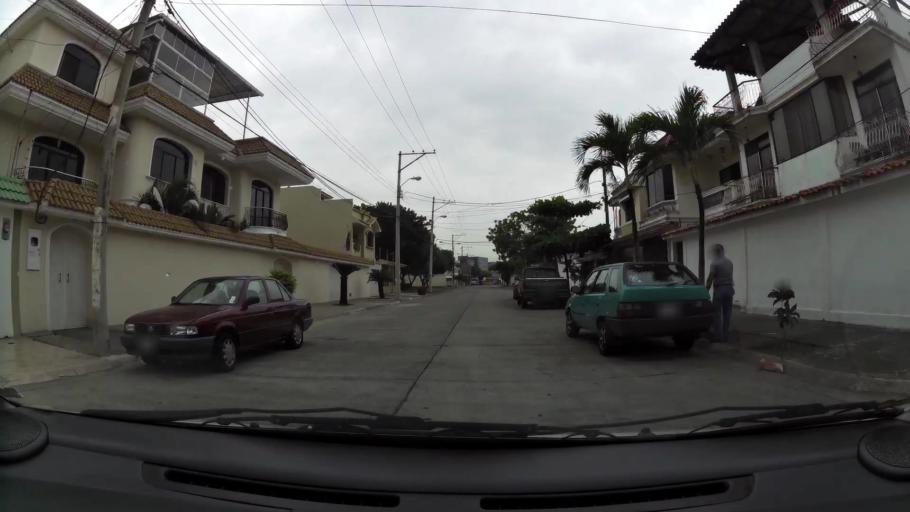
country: EC
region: Guayas
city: Eloy Alfaro
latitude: -2.1484
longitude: -79.8892
